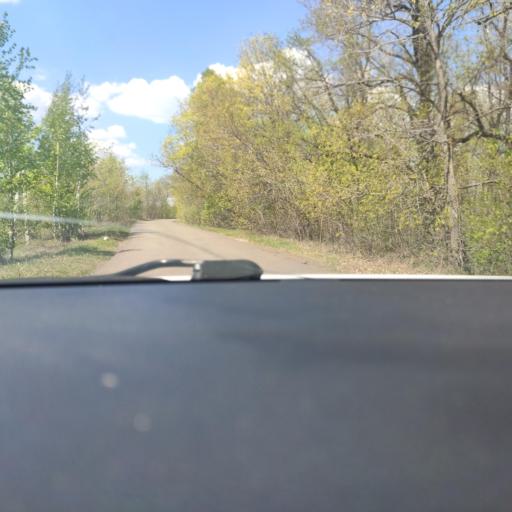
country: RU
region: Bashkortostan
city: Avdon
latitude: 54.6128
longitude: 55.6219
